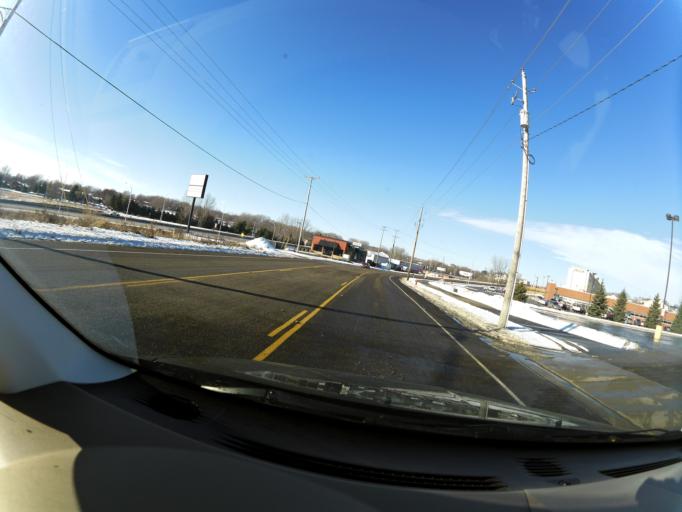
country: US
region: Minnesota
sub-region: Olmsted County
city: Rochester
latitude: 44.0814
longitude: -92.5075
